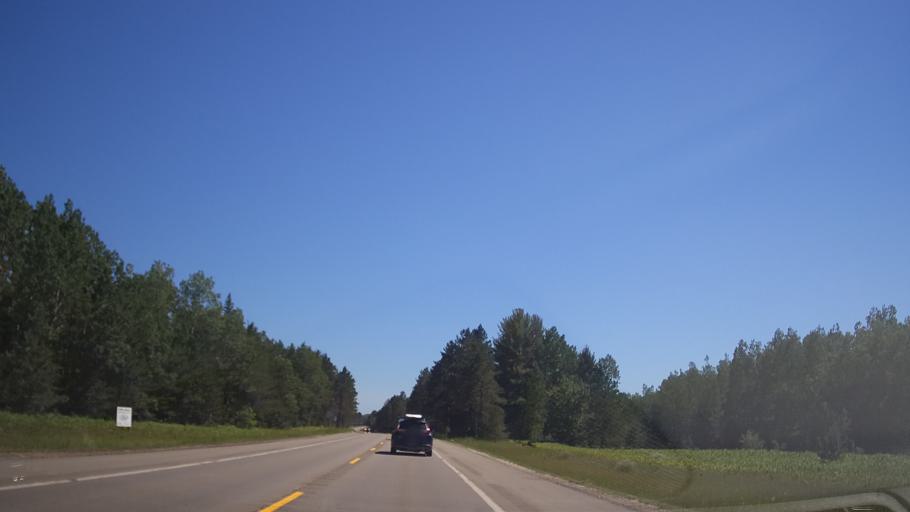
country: US
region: Michigan
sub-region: Cheboygan County
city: Indian River
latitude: 45.5461
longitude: -84.7843
